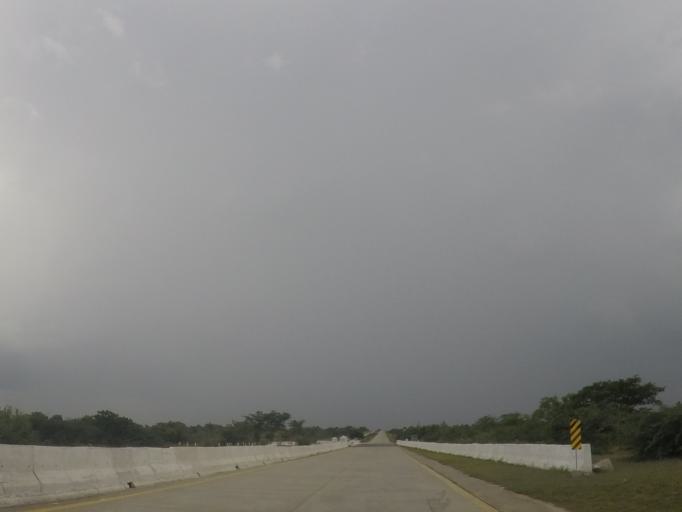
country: MM
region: Mandalay
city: Meiktila
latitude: 21.0472
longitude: 95.7868
